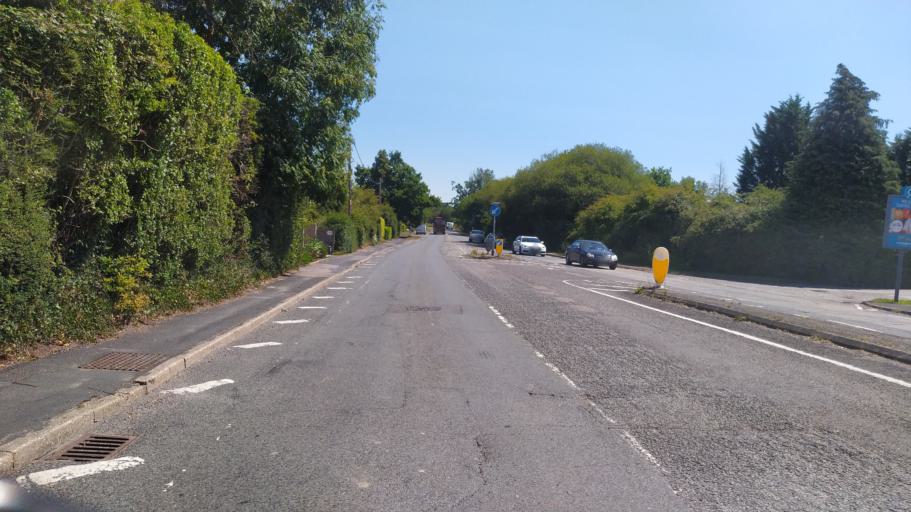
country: GB
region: England
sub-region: Hampshire
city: Cadnam
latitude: 50.9178
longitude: -1.5647
